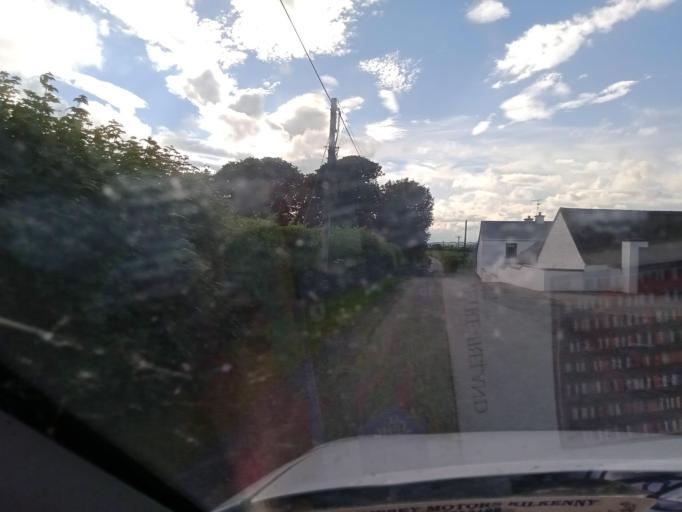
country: IE
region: Leinster
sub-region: Laois
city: Rathdowney
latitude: 52.7750
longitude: -7.5253
